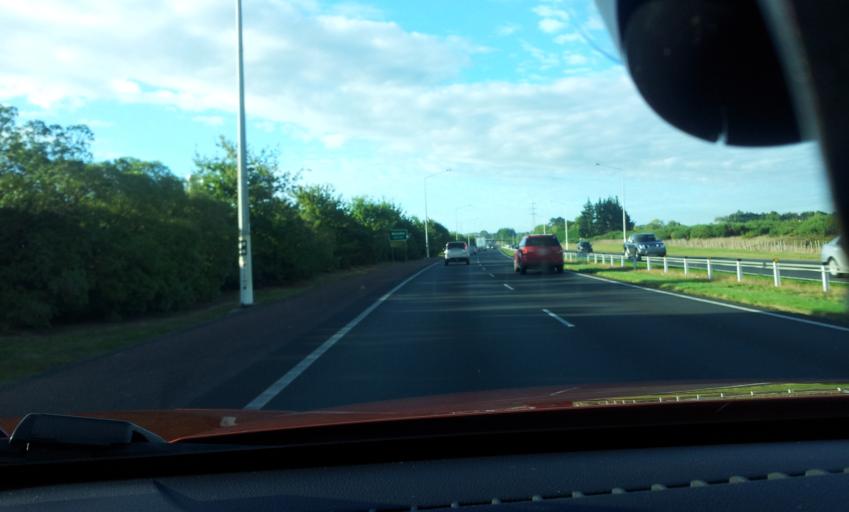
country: NZ
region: Auckland
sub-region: Auckland
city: Papakura
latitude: -37.0963
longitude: 174.9448
